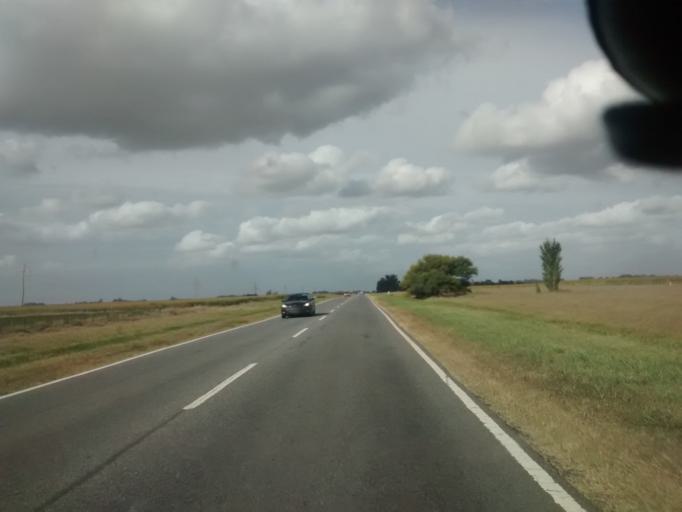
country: AR
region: Buenos Aires
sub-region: Partido de Balcarce
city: Balcarce
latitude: -37.6702
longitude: -58.5108
